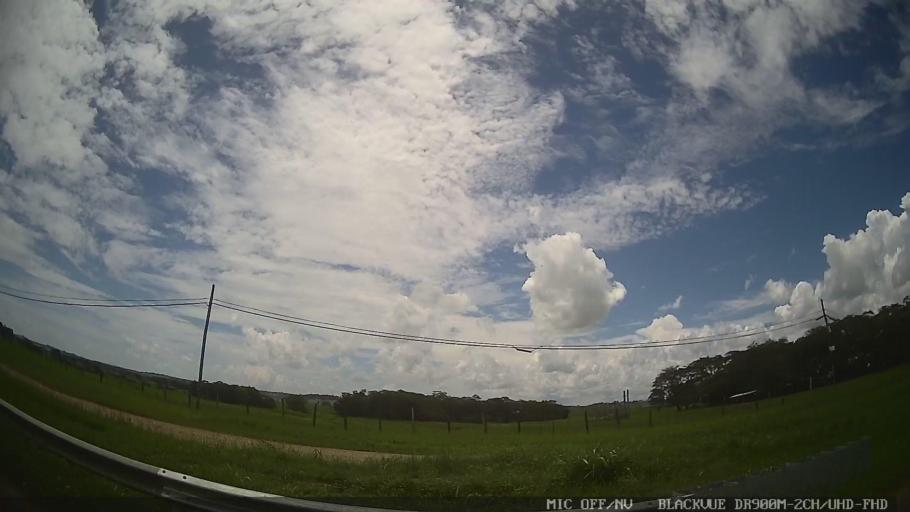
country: BR
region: Sao Paulo
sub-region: Conchas
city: Conchas
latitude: -23.0464
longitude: -47.9541
